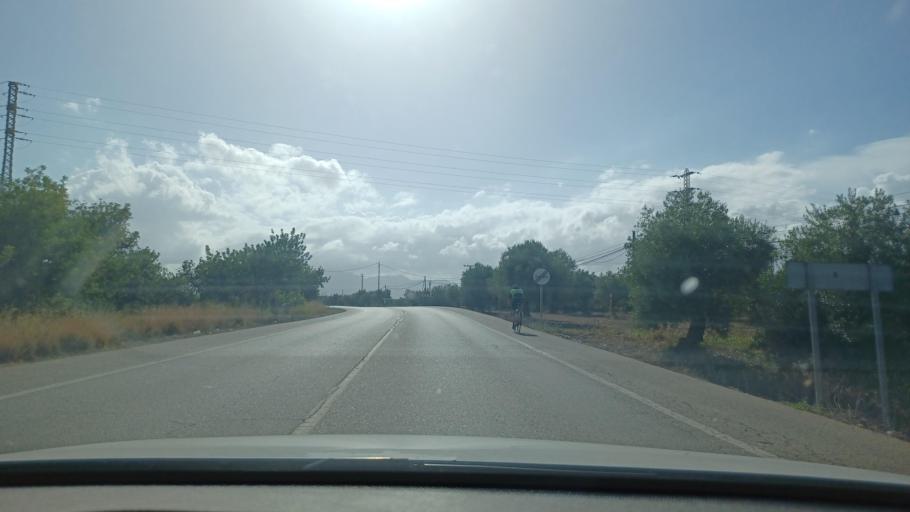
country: ES
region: Catalonia
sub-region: Provincia de Tarragona
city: Cambrils
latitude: 41.0465
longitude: 0.9924
